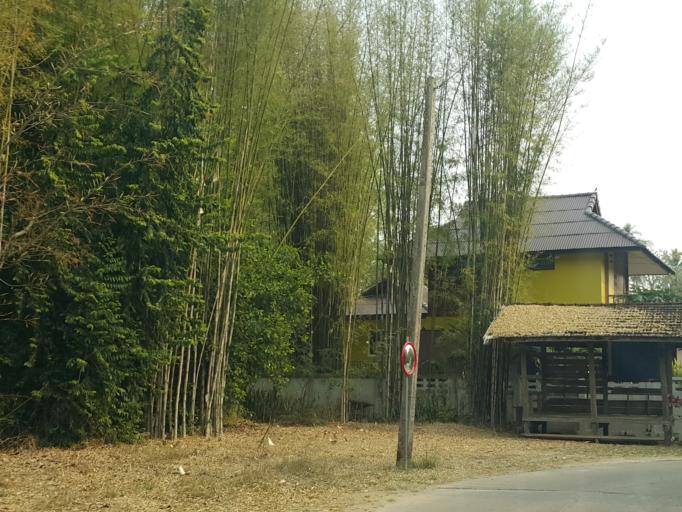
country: TH
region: Chiang Mai
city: Mae Taeng
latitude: 18.9541
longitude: 98.9188
